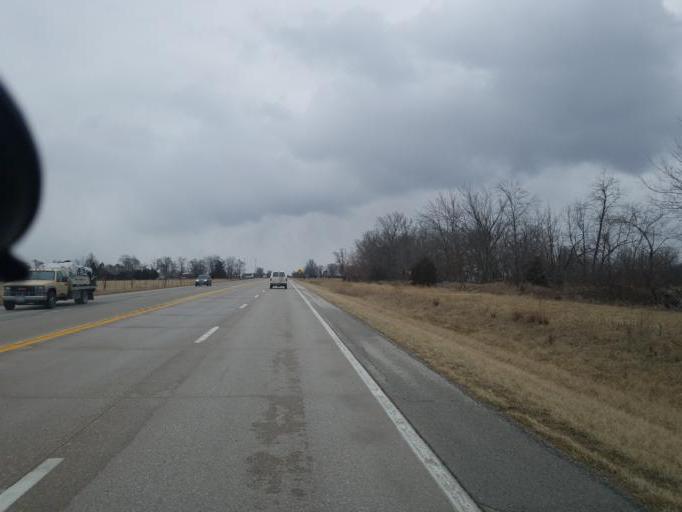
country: US
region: Missouri
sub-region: Macon County
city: Macon
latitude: 39.7793
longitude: -92.4787
